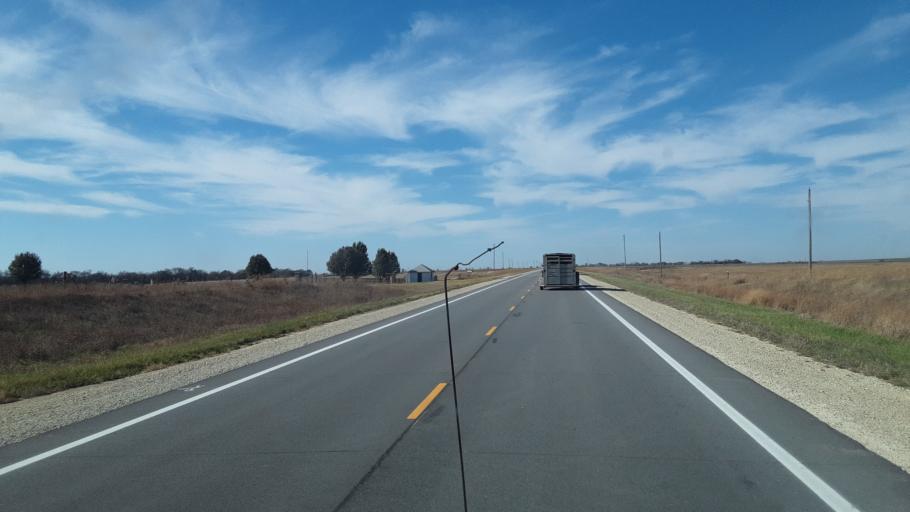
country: US
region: Kansas
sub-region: Marion County
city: Marion
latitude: 38.3629
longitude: -96.8827
